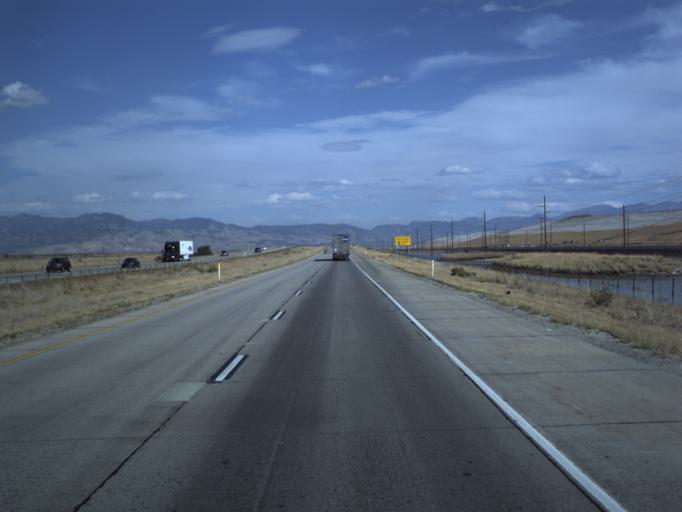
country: US
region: Utah
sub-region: Salt Lake County
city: Magna
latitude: 40.7706
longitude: -112.1469
